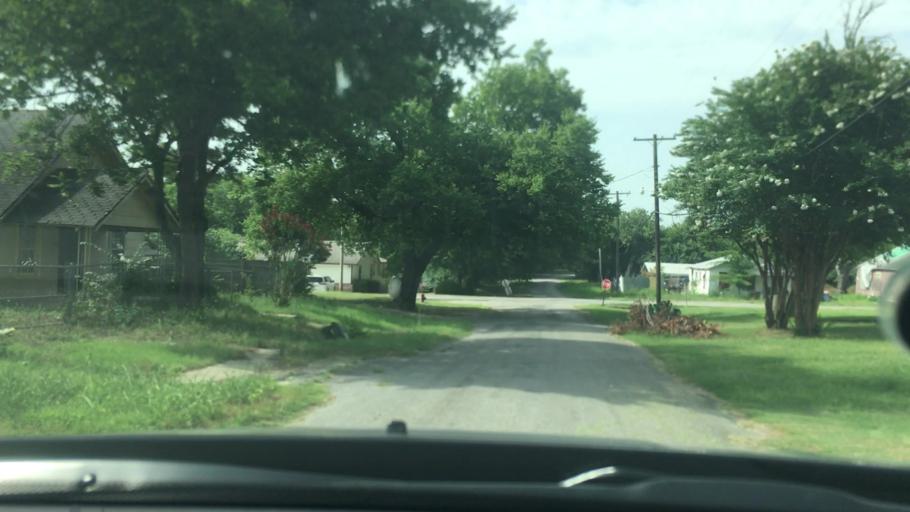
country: US
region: Oklahoma
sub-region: Garvin County
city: Pauls Valley
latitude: 34.8275
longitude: -97.2579
